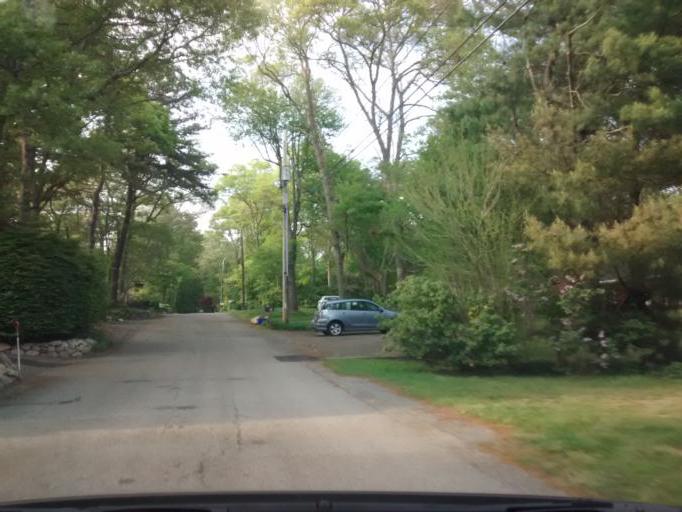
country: US
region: Massachusetts
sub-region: Barnstable County
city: East Falmouth
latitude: 41.5965
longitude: -70.5794
